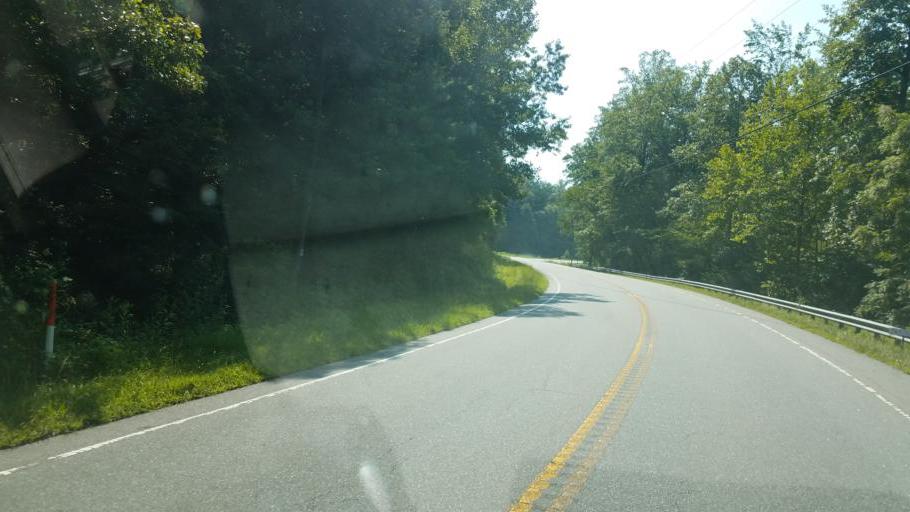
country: US
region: North Carolina
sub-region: Burke County
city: Glen Alpine
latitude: 35.8654
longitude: -81.7937
